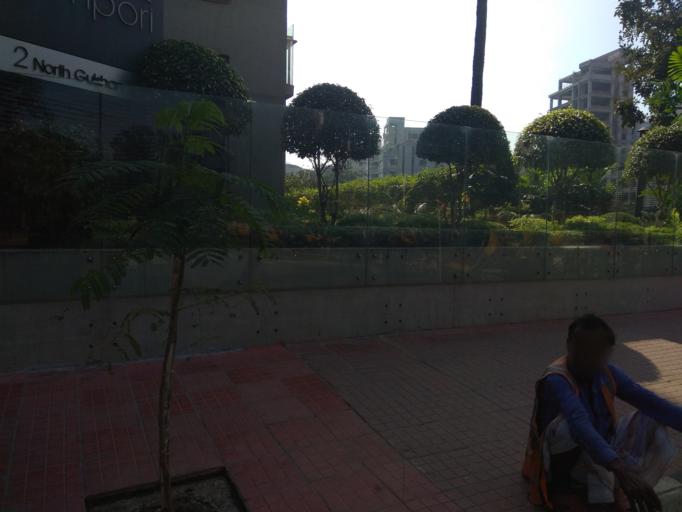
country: BD
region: Dhaka
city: Paltan
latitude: 23.8004
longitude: 90.4081
